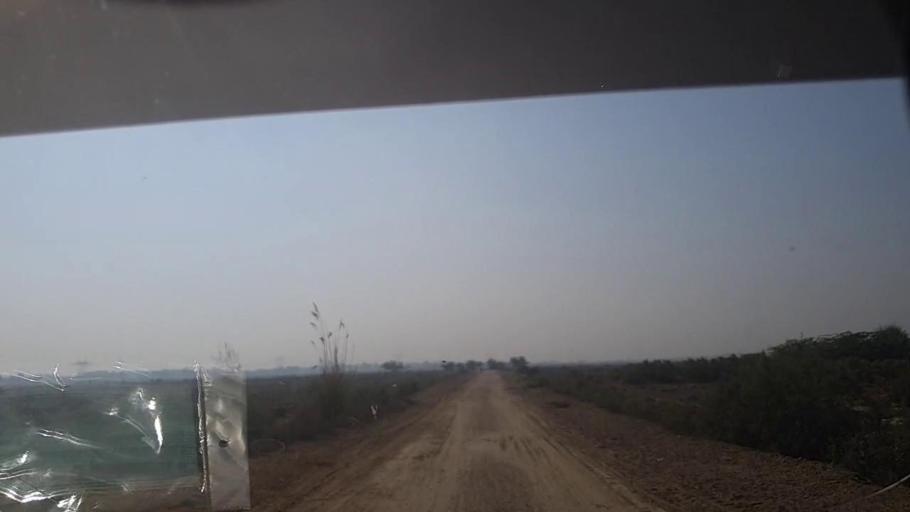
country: PK
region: Sindh
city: Khairpur
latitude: 27.4626
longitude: 68.7387
